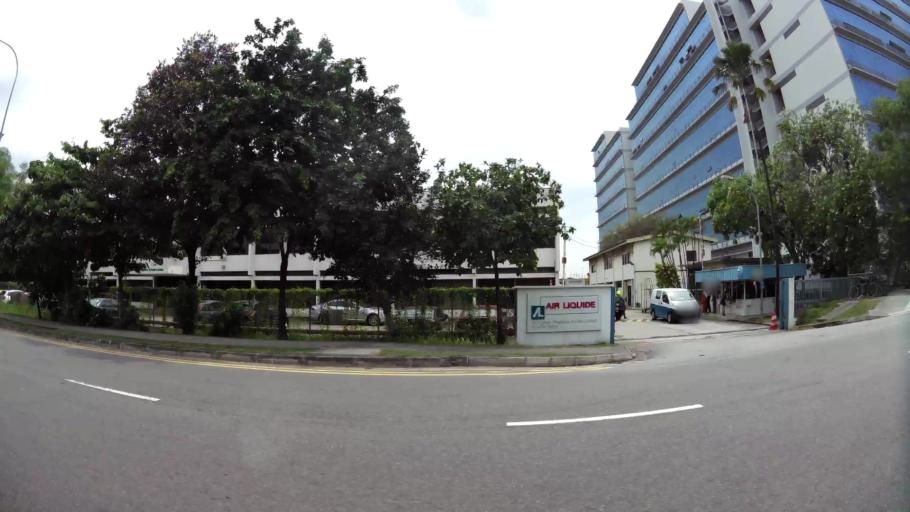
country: SG
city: Singapore
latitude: 1.3136
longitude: 103.7032
